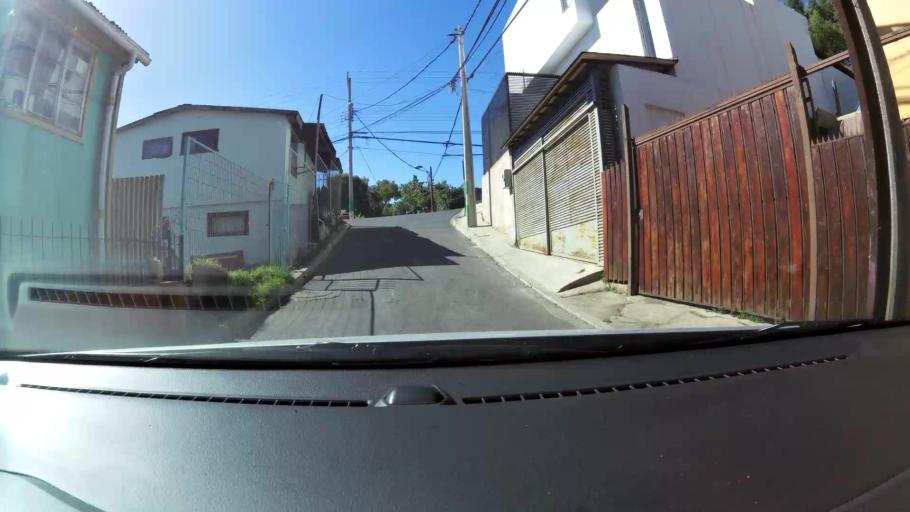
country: CL
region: Valparaiso
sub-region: Provincia de Valparaiso
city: Vina del Mar
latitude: -33.0337
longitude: -71.5715
